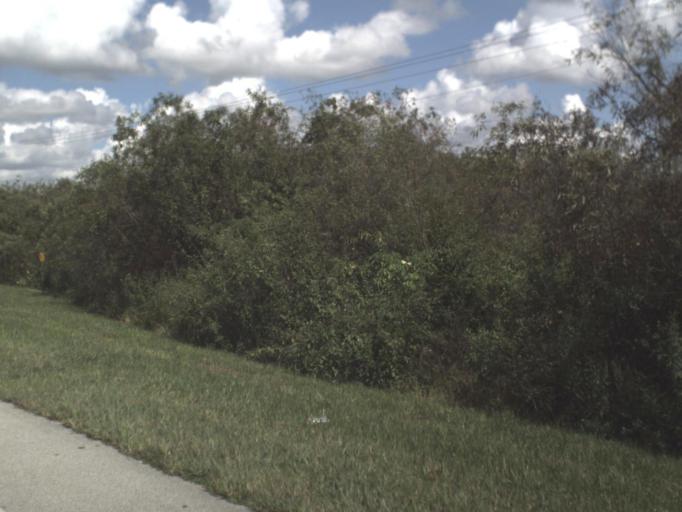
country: US
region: Florida
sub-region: Collier County
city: Immokalee
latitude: 26.4842
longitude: -81.4346
